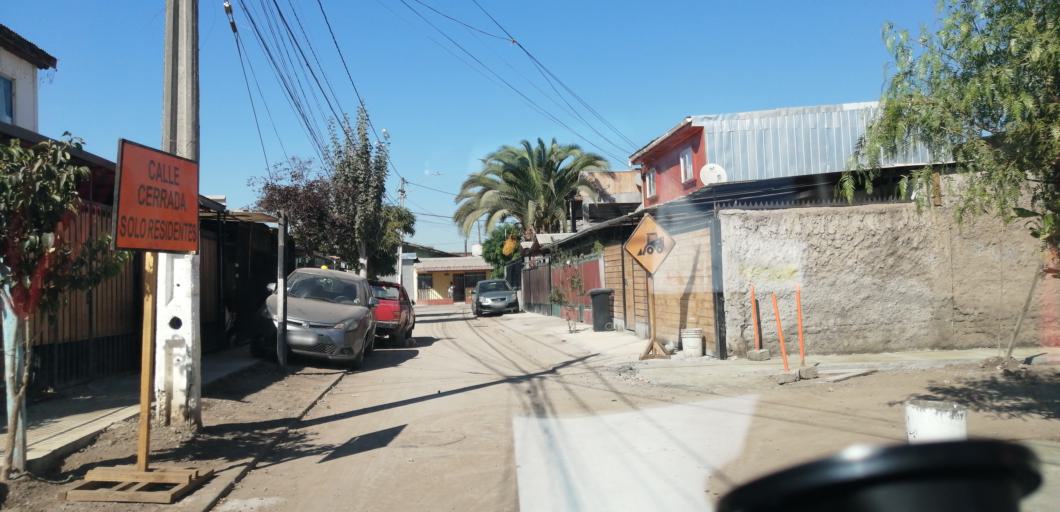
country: CL
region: Santiago Metropolitan
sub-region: Provincia de Santiago
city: Lo Prado
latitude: -33.4386
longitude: -70.7575
